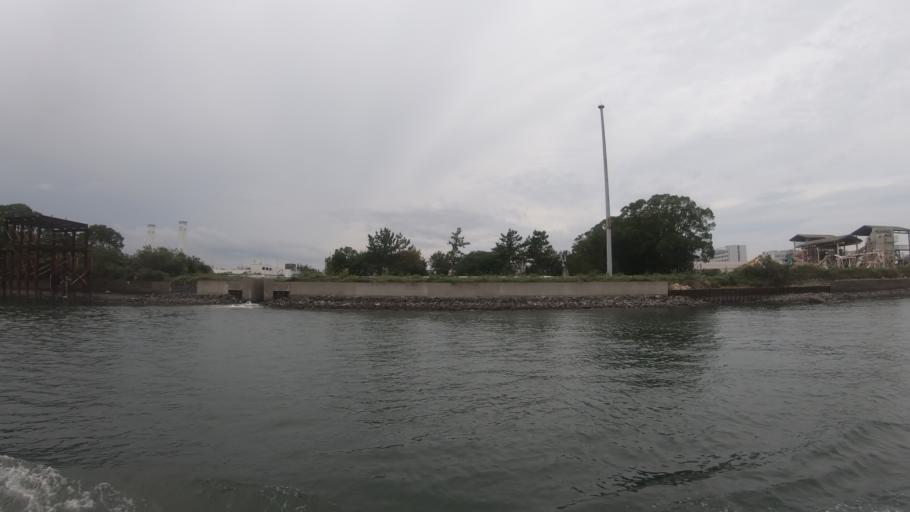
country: JP
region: Kanagawa
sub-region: Kawasaki-shi
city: Kawasaki
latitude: 35.4885
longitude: 139.6896
